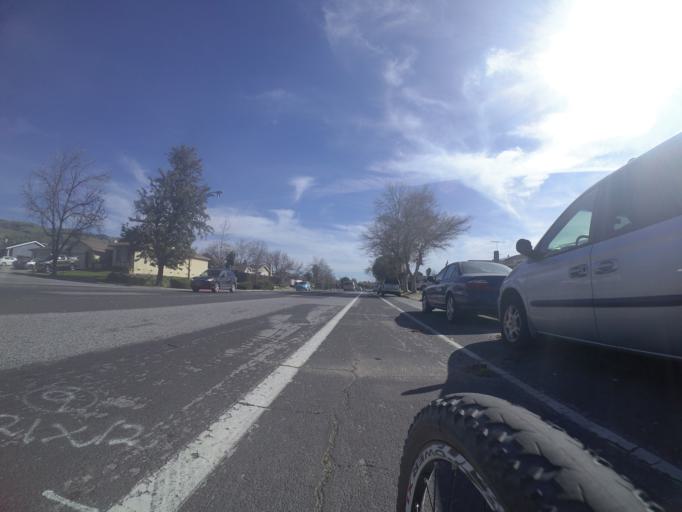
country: US
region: California
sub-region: Santa Clara County
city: Milpitas
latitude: 37.4178
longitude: -121.8580
